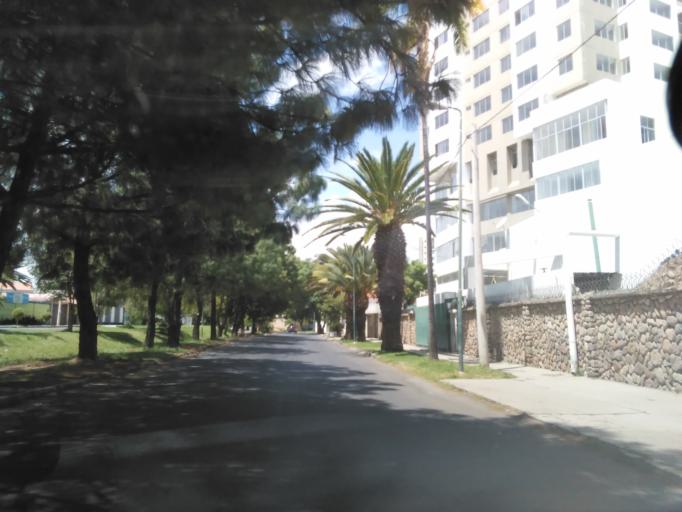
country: BO
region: Cochabamba
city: Cochabamba
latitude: -17.3719
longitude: -66.1510
